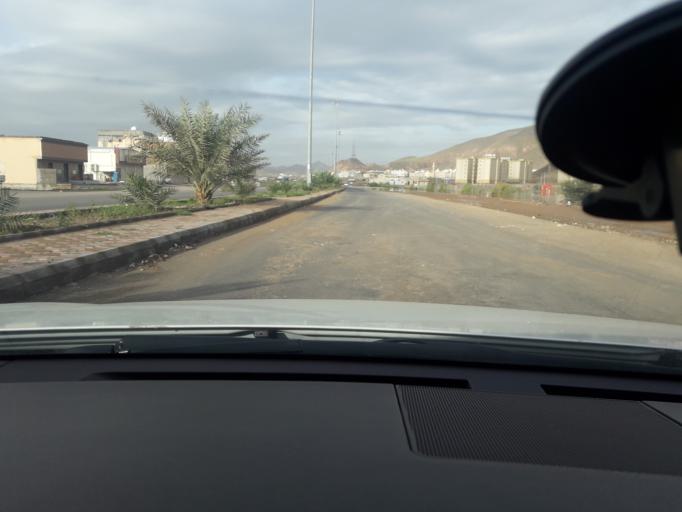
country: SA
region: Al Madinah al Munawwarah
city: Sultanah
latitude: 24.4678
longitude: 39.4942
